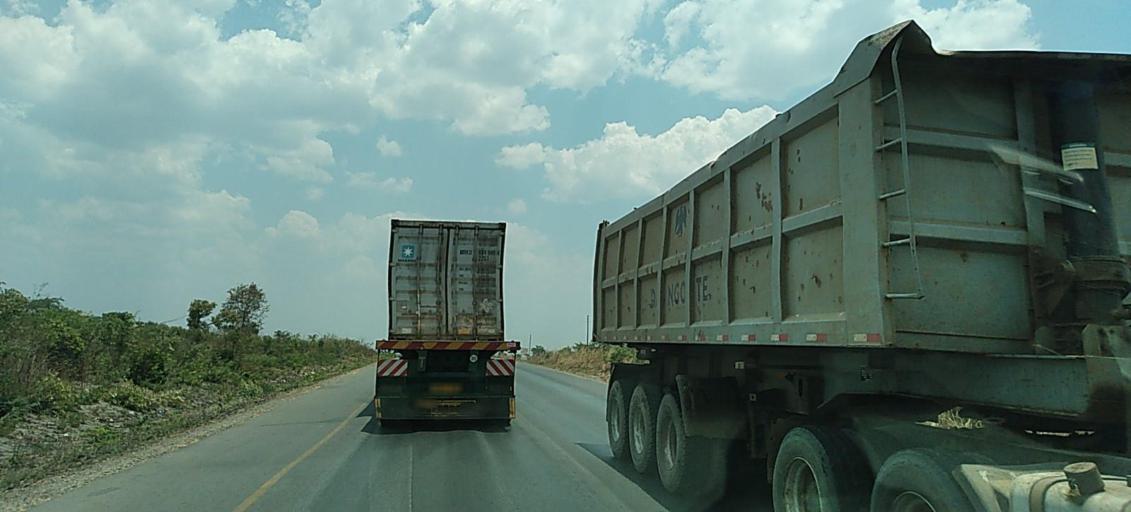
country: ZM
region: Central
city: Kapiri Mposhi
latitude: -14.0494
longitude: 28.6534
